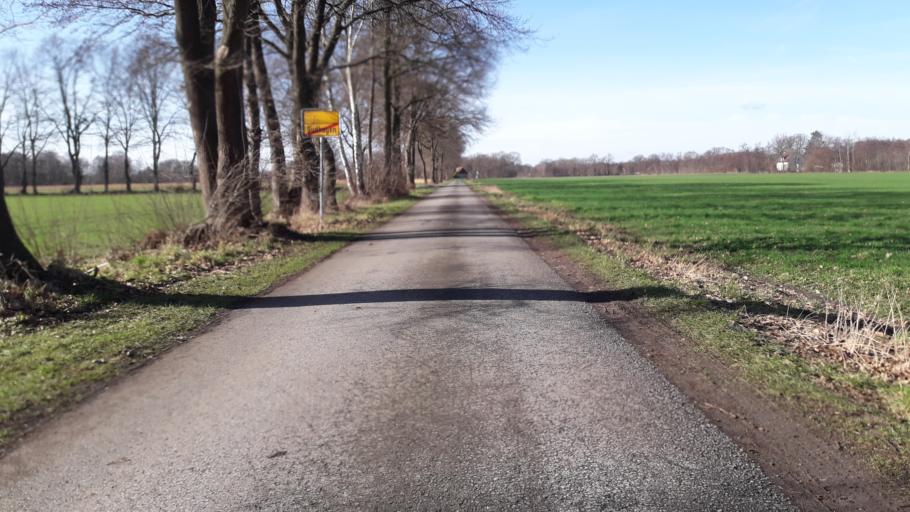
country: DE
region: North Rhine-Westphalia
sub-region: Regierungsbezirk Detmold
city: Delbruck
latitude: 51.7441
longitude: 8.4986
